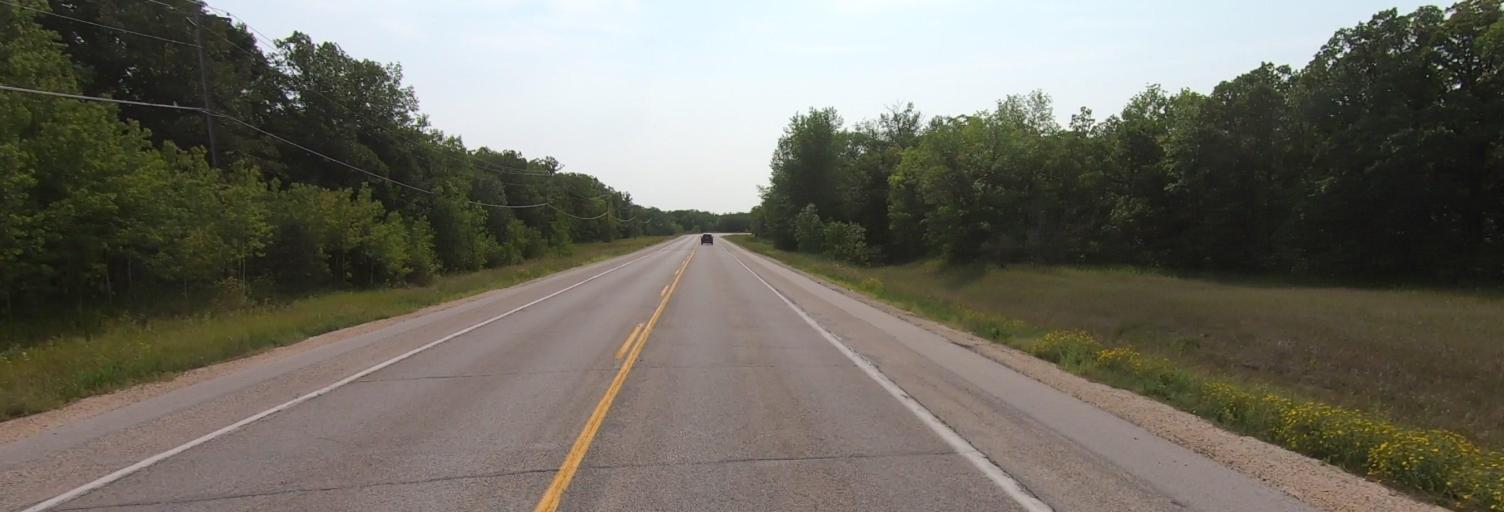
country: CA
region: Manitoba
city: Niverville
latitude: 49.7296
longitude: -97.0960
